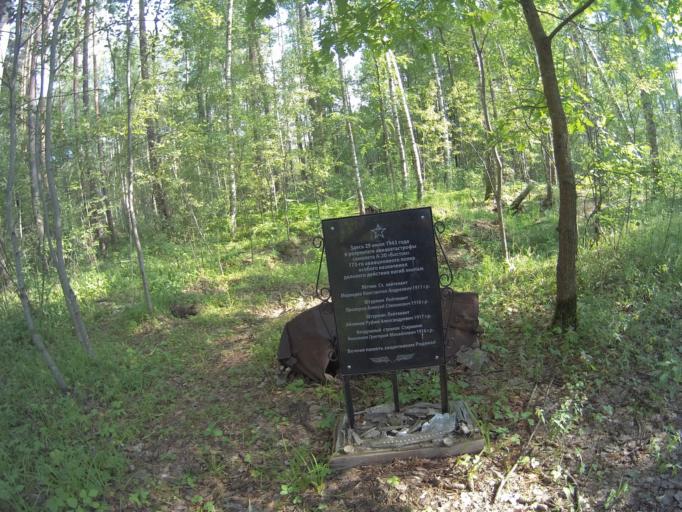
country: RU
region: Vladimir
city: Orgtrud
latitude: 56.2889
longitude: 40.7063
